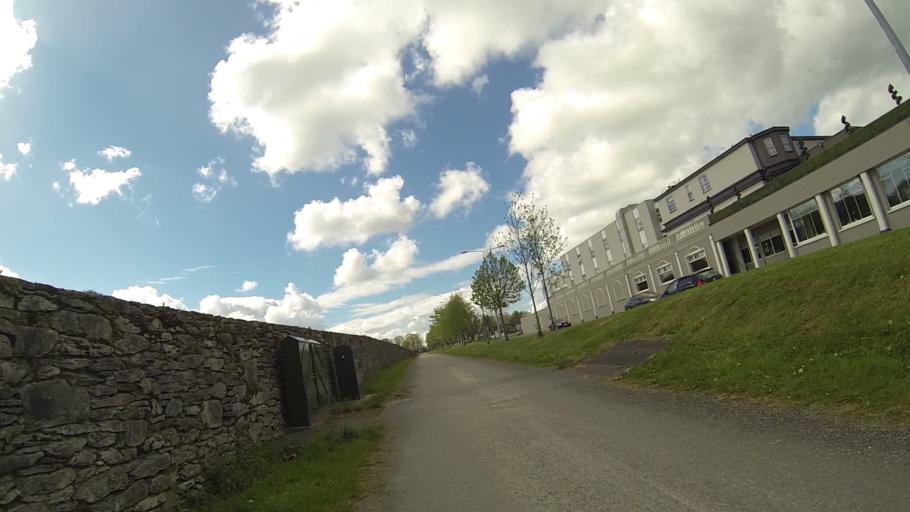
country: IE
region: Munster
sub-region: Ciarrai
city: Cill Airne
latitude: 52.0437
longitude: -9.5019
